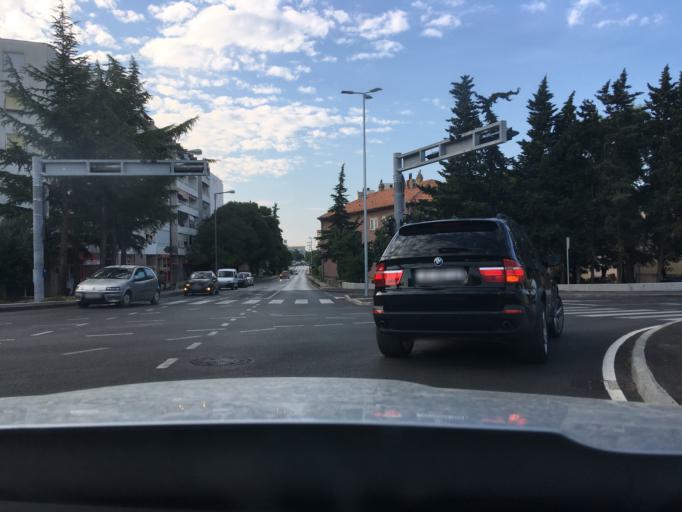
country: HR
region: Zadarska
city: Zadar
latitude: 44.1264
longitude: 15.2343
